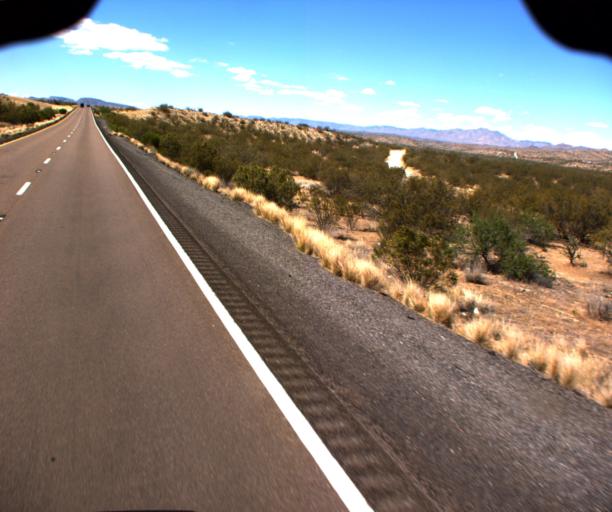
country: US
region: Arizona
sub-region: Mohave County
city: Kingman
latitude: 35.0424
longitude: -113.6645
